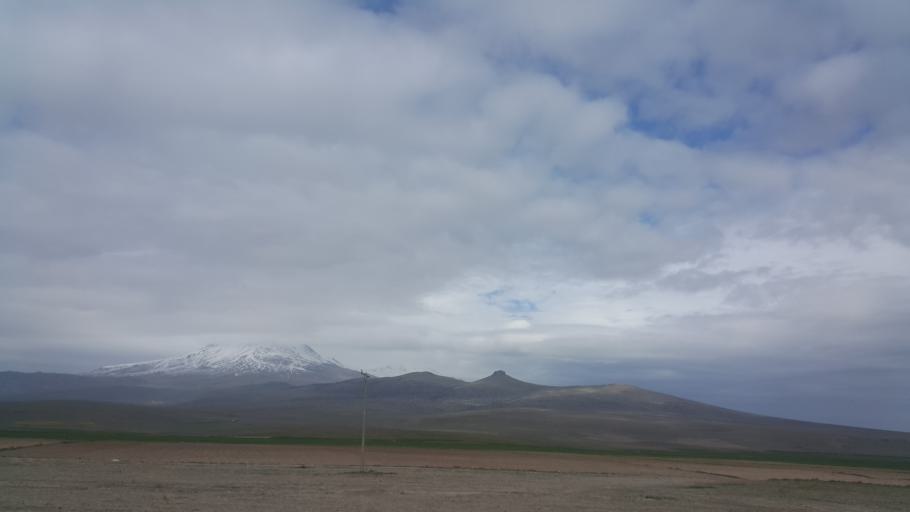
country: TR
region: Aksaray
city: Taspinar
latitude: 38.0437
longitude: 34.0352
